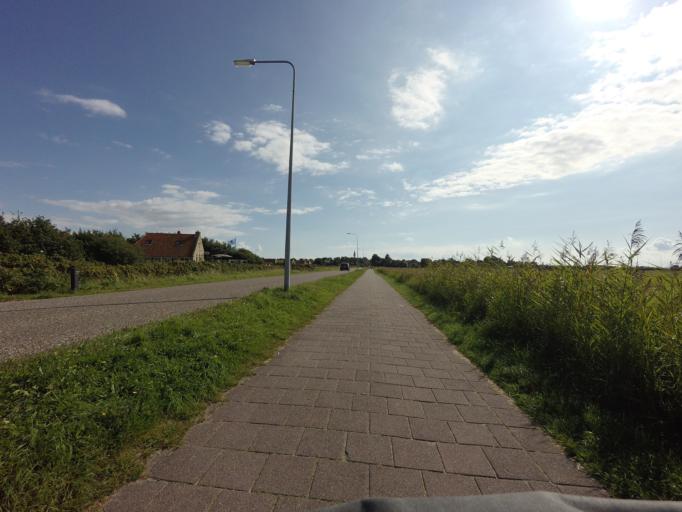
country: NL
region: Friesland
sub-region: Gemeente Terschelling
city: West-Terschelling
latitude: 53.3877
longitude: 5.2845
